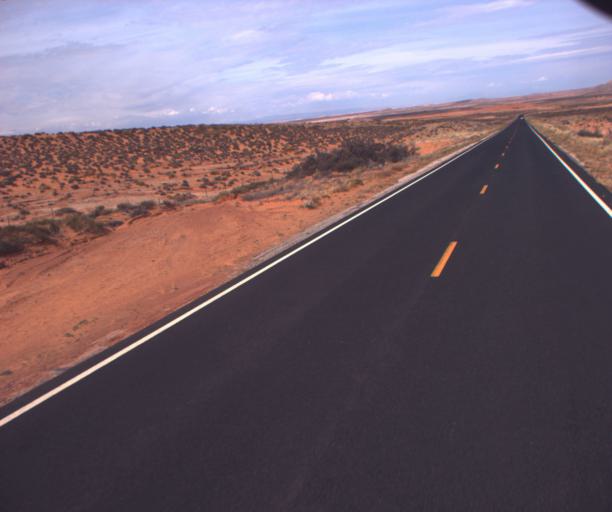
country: US
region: Arizona
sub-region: Apache County
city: Many Farms
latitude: 36.9006
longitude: -109.6253
